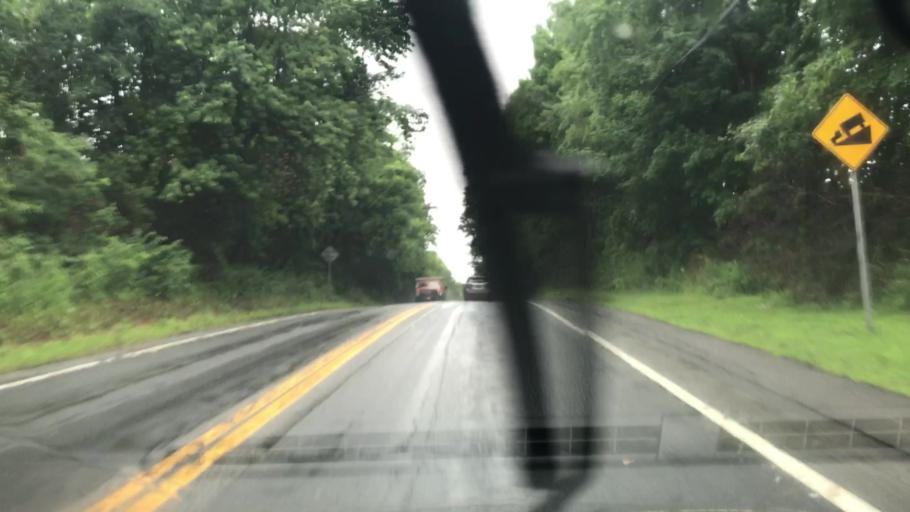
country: US
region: New York
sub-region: Westchester County
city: Jefferson Valley-Yorktown
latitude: 41.3374
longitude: -73.7749
